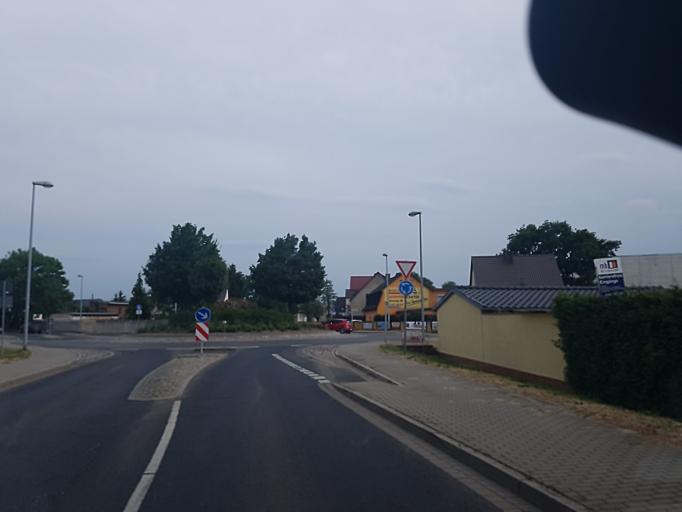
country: DE
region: Saxony-Anhalt
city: Wittenburg
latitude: 51.8790
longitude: 12.6316
